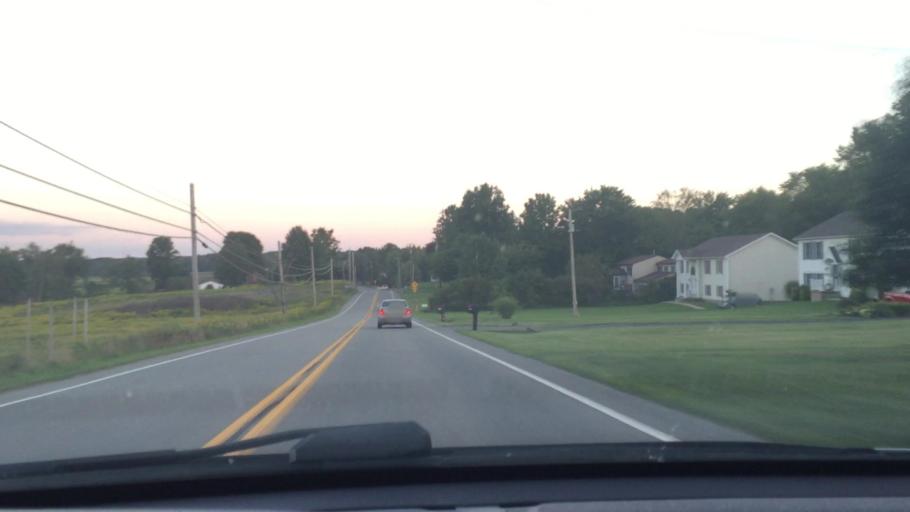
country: US
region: Pennsylvania
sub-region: Mercer County
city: Grove City
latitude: 41.1379
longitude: -80.0776
